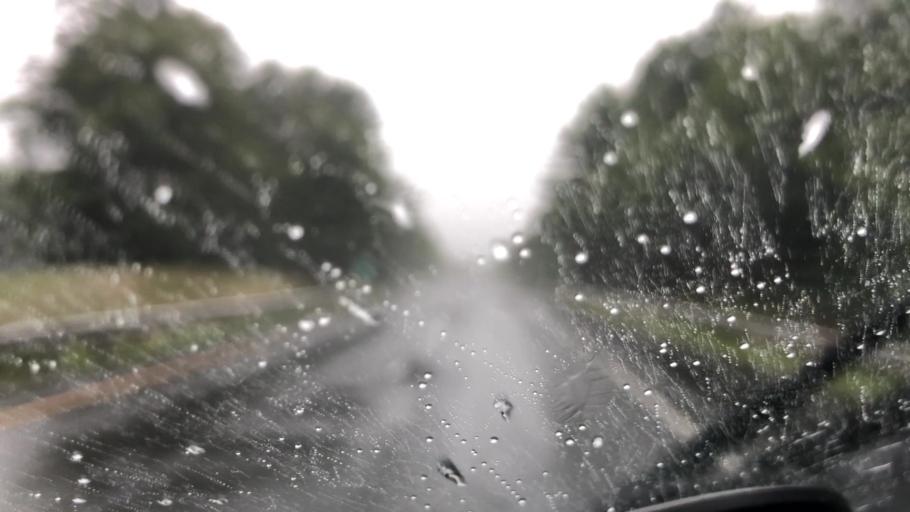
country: US
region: Massachusetts
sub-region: Hampden County
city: Westfield
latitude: 42.1562
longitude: -72.7785
